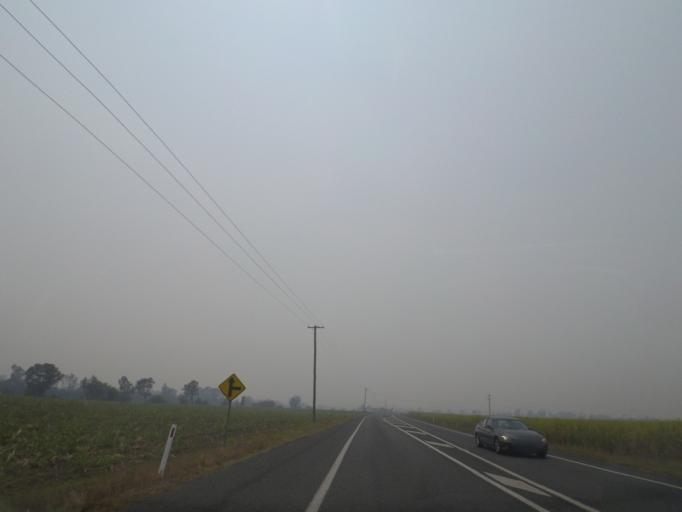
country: AU
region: New South Wales
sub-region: Clarence Valley
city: Maclean
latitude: -29.5645
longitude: 153.1095
